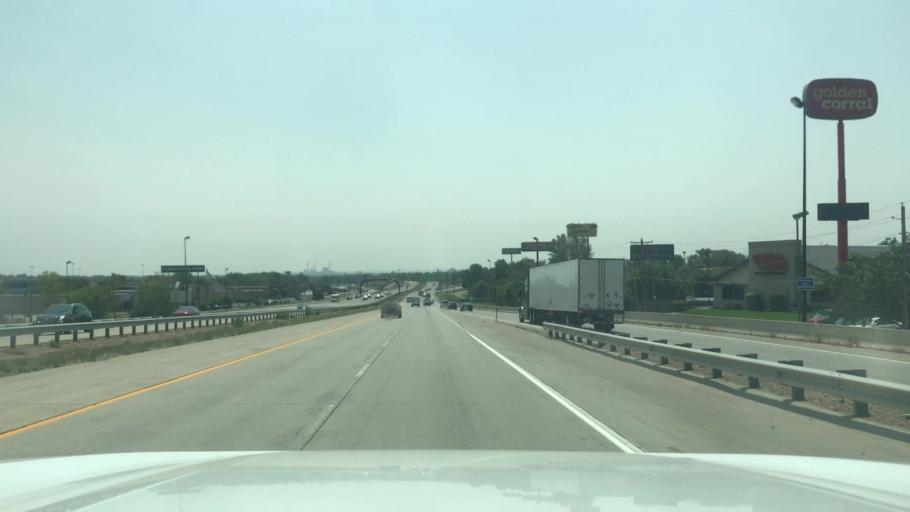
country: US
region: Colorado
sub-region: Pueblo County
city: Pueblo
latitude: 38.3058
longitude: -104.6135
